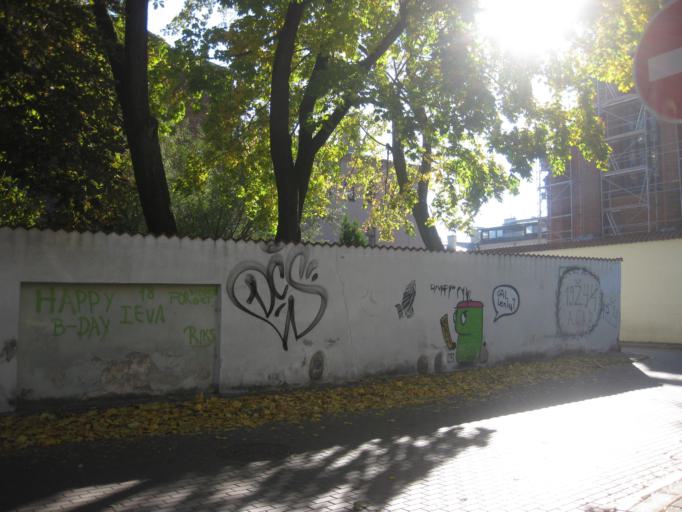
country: LT
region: Kauno apskritis
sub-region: Kaunas
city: Kaunas
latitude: 54.8978
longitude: 23.8888
